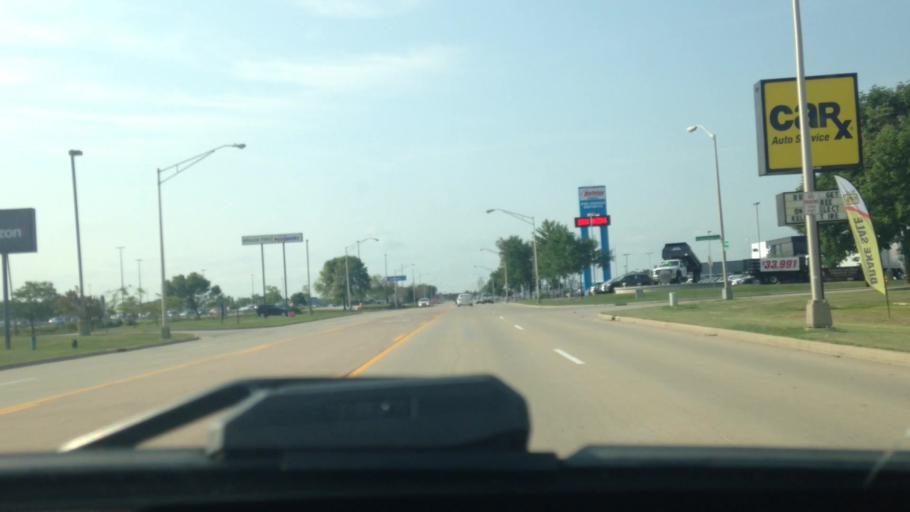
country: US
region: Wisconsin
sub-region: Fond du Lac County
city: North Fond du Lac
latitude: 43.7904
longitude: -88.4866
